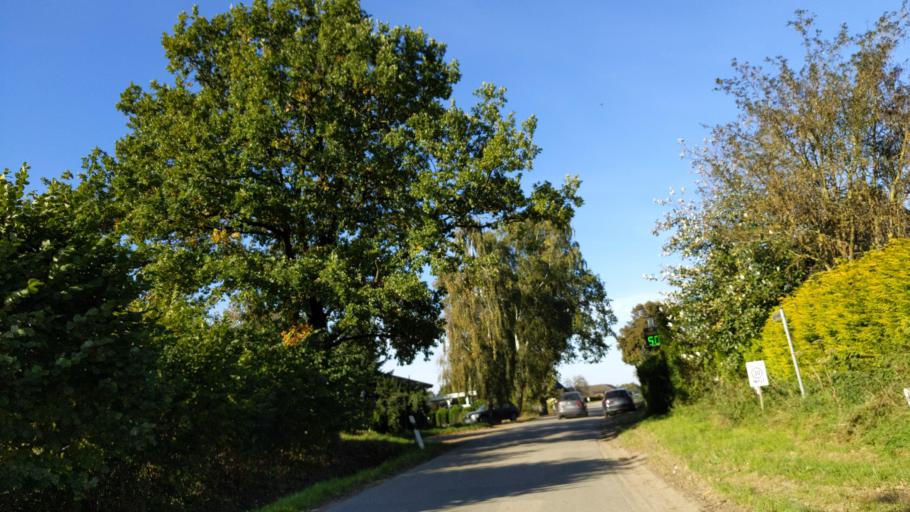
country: DE
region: Schleswig-Holstein
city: Ahrensbok
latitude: 54.0511
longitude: 10.5988
